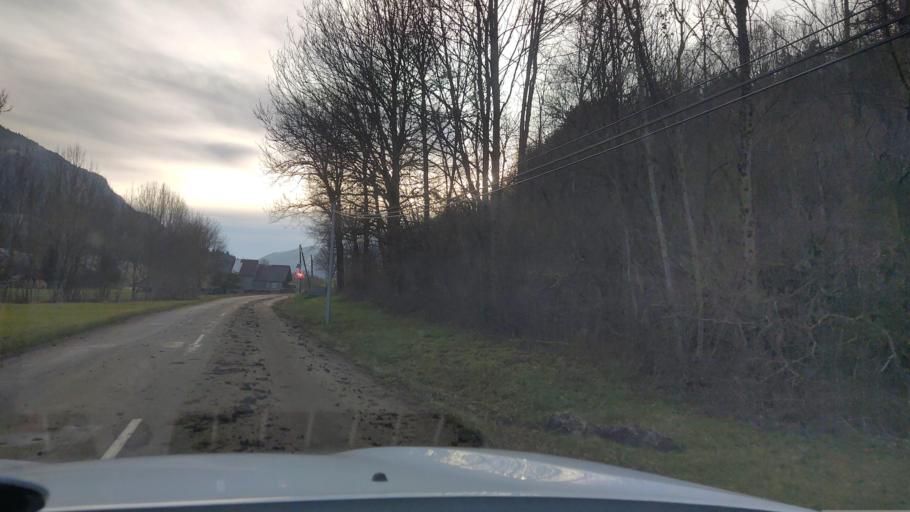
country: FR
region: Rhone-Alpes
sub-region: Departement de la Savoie
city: Gresy-sur-Isere
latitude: 45.6345
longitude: 6.1589
